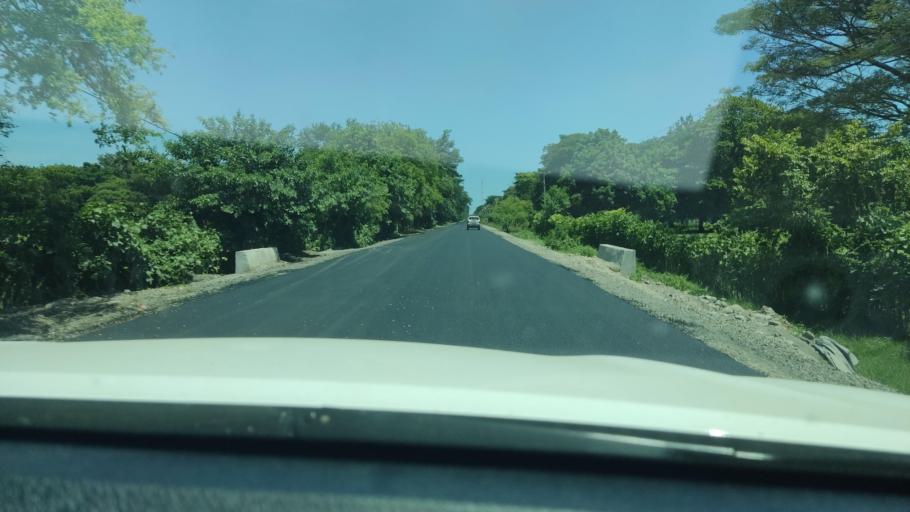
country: SV
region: Ahuachapan
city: San Francisco Menendez
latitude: 13.8365
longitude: -90.1199
